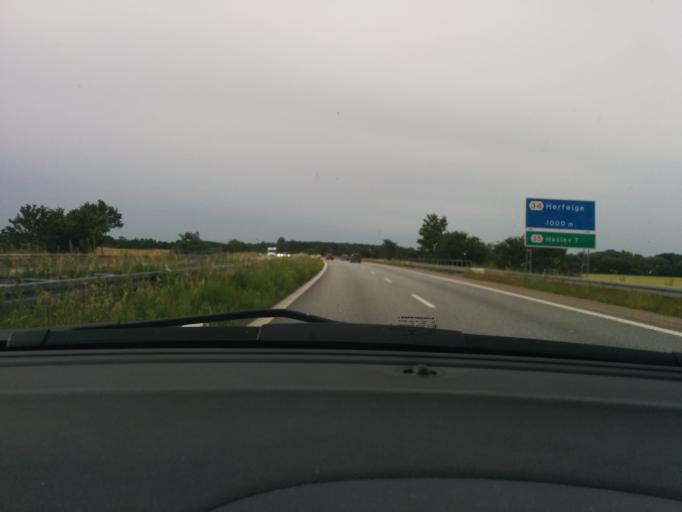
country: DK
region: Zealand
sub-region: Koge Kommune
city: Bjaeverskov
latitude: 55.4001
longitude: 12.0962
